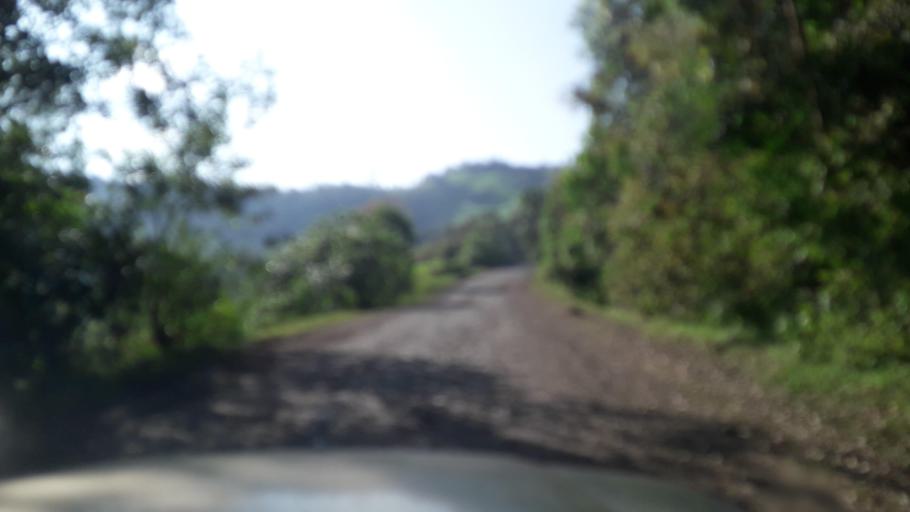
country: ET
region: Oromiya
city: Jima
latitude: 7.4388
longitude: 36.8711
